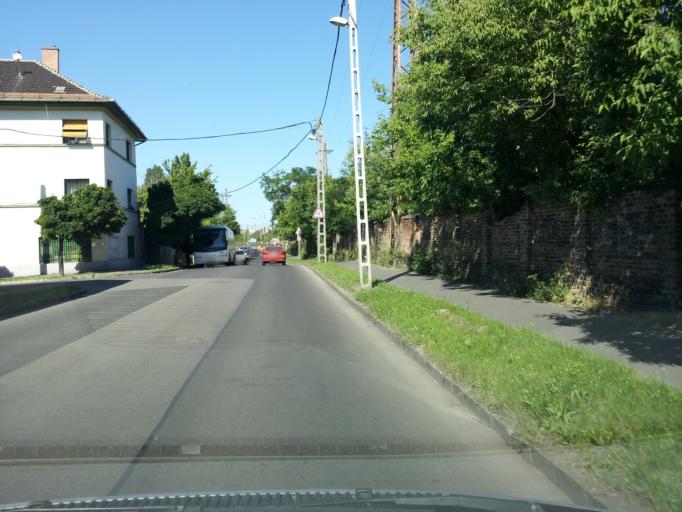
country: HU
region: Budapest
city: Budapest XIII. keruelet
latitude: 47.5246
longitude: 19.0875
